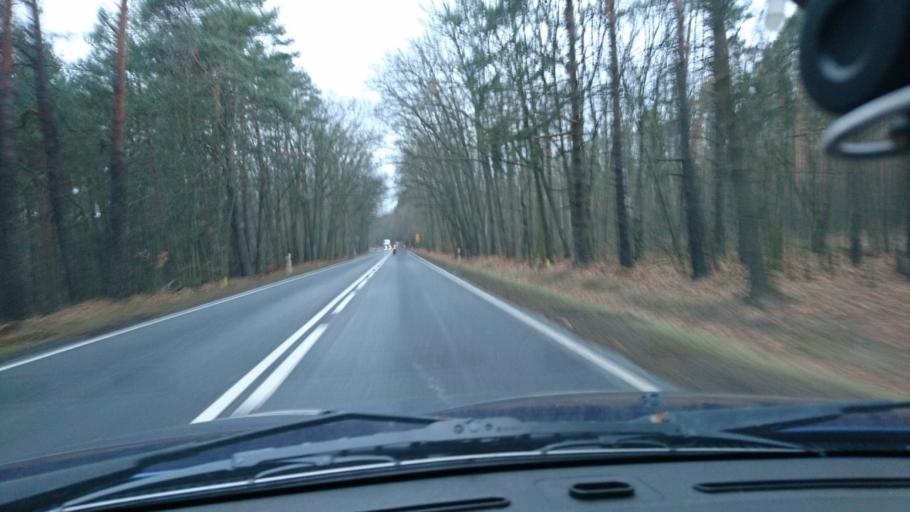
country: PL
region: Opole Voivodeship
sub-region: Powiat kluczborski
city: Kluczbork
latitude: 50.9588
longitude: 18.3045
